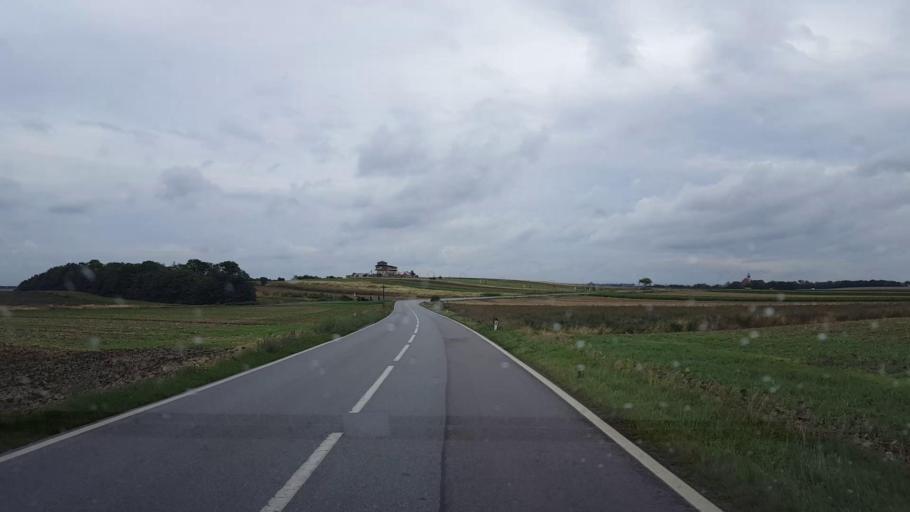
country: AT
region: Lower Austria
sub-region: Politischer Bezirk Wien-Umgebung
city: Rauchenwarth
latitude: 48.0830
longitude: 16.4982
